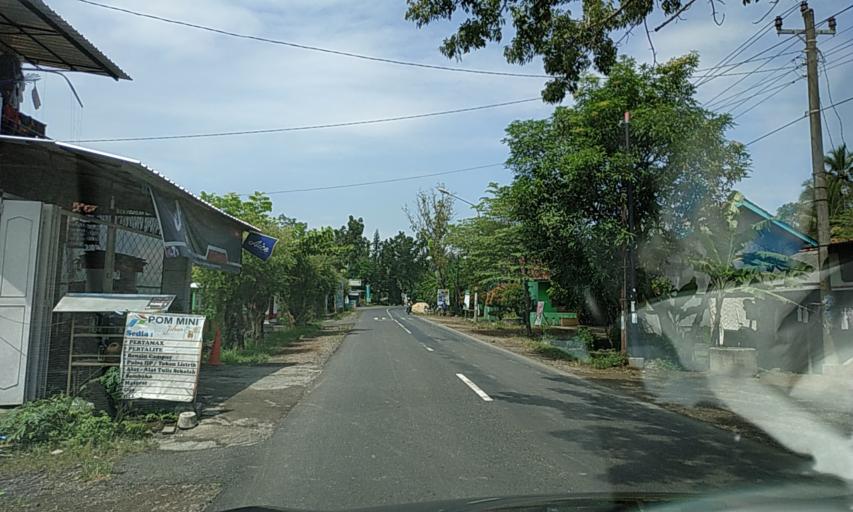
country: ID
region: Central Java
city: Mulyosari
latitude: -7.5155
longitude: 108.7841
